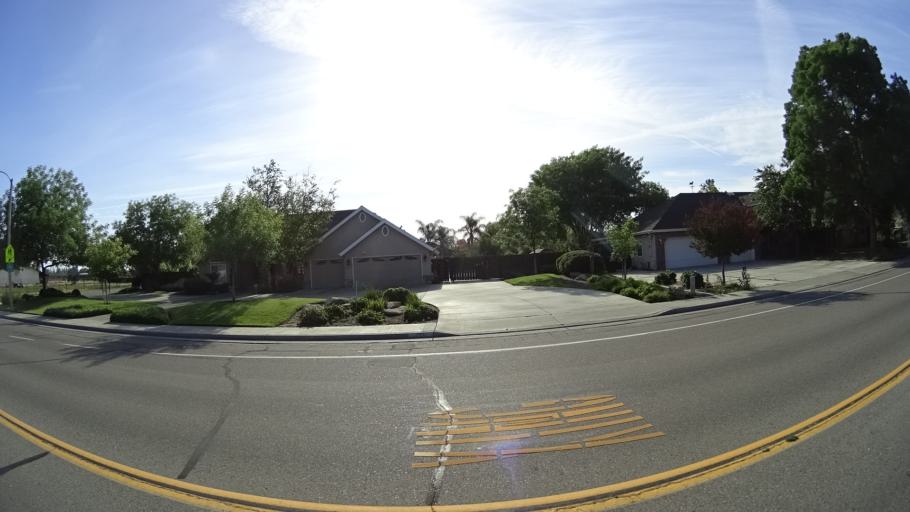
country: US
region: California
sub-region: Kings County
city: Lucerne
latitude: 36.3654
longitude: -119.6461
